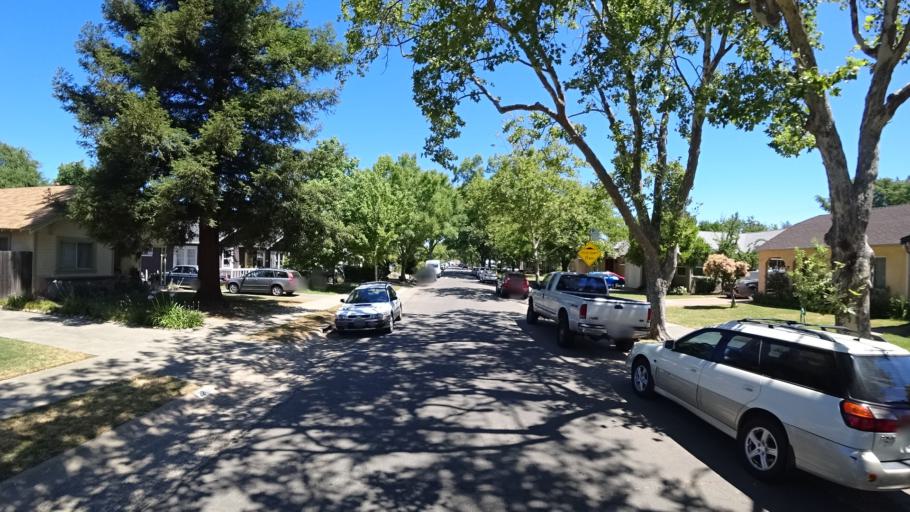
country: US
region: California
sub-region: Sacramento County
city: Sacramento
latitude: 38.5567
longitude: -121.4632
